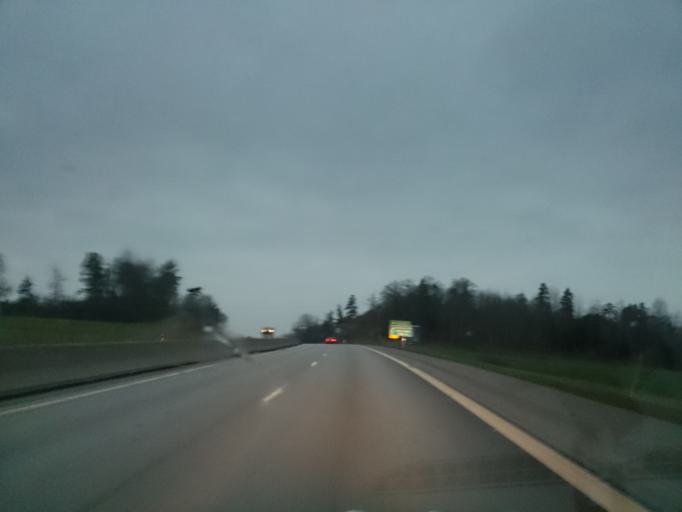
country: SE
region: OEstergoetland
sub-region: Norrkopings Kommun
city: Kimstad
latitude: 58.5309
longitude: 16.0259
